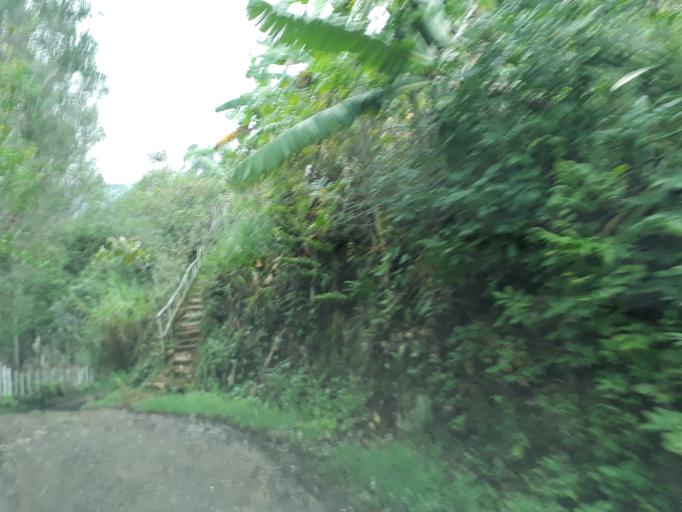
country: CO
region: Cundinamarca
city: Manta
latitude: 5.0604
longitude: -73.5241
